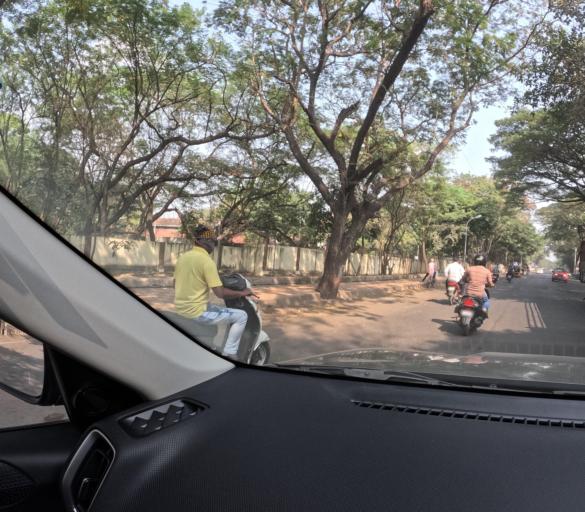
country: IN
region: Maharashtra
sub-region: Pune Division
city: Pune
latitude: 18.5240
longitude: 73.8904
